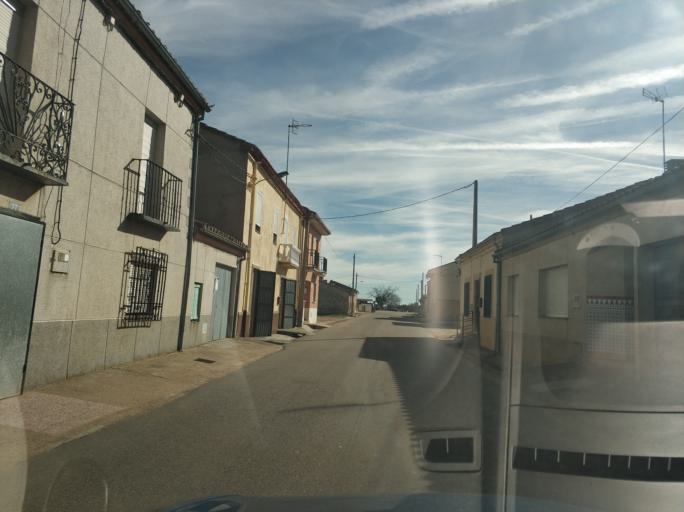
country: ES
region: Castille and Leon
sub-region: Provincia de Zamora
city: Cuelgamures
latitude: 41.2547
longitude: -5.7101
